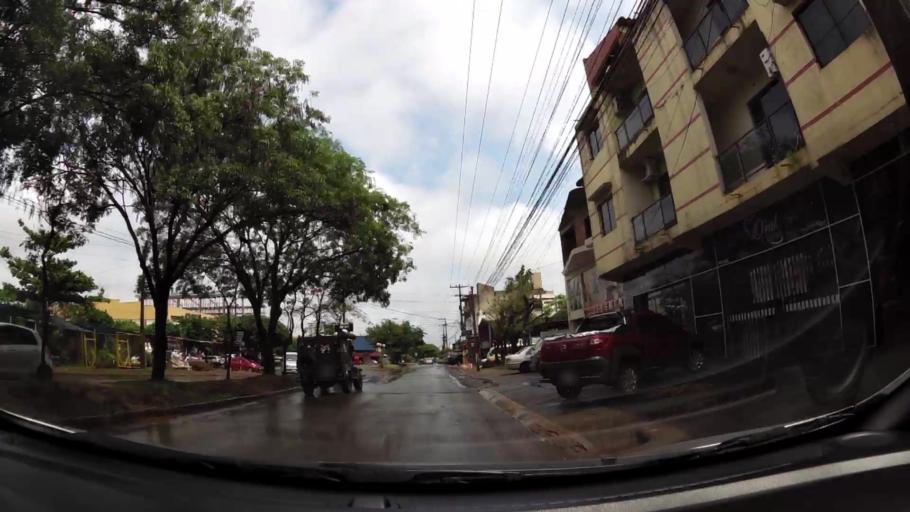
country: PY
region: Alto Parana
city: Presidente Franco
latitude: -25.5126
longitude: -54.6532
